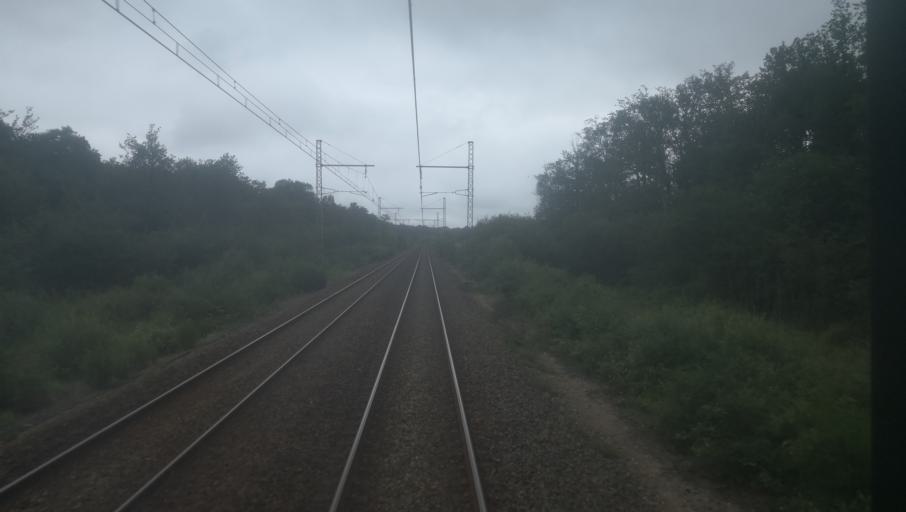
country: FR
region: Centre
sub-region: Departement de l'Indre
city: Luant
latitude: 46.7469
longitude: 1.5944
